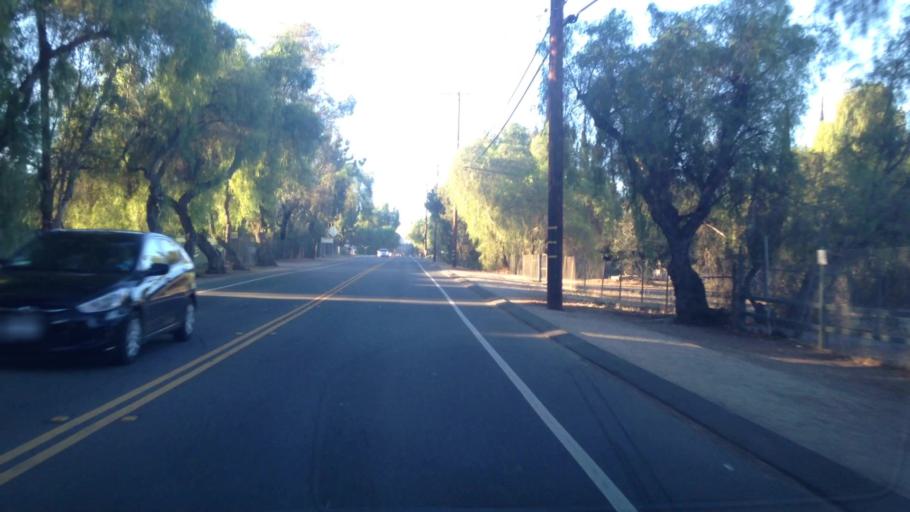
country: US
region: California
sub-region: Riverside County
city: Woodcrest
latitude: 33.8786
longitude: -117.3662
